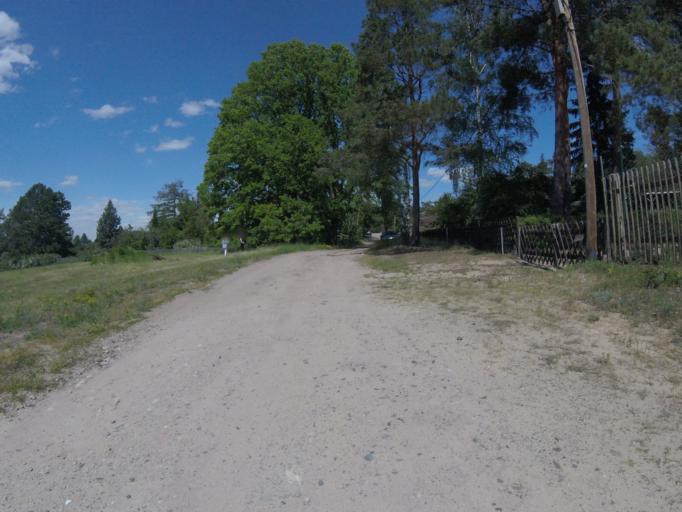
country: DE
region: Brandenburg
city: Schwerin
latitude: 52.1386
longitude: 13.6293
